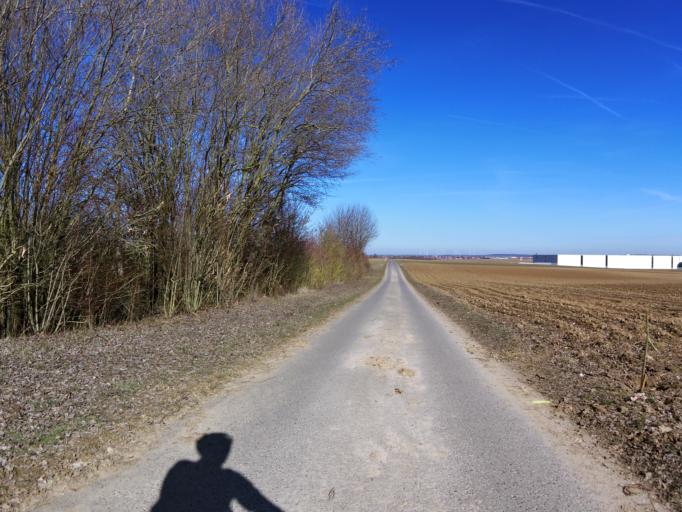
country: DE
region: Bavaria
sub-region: Regierungsbezirk Unterfranken
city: Kurnach
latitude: 49.8501
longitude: 10.0187
